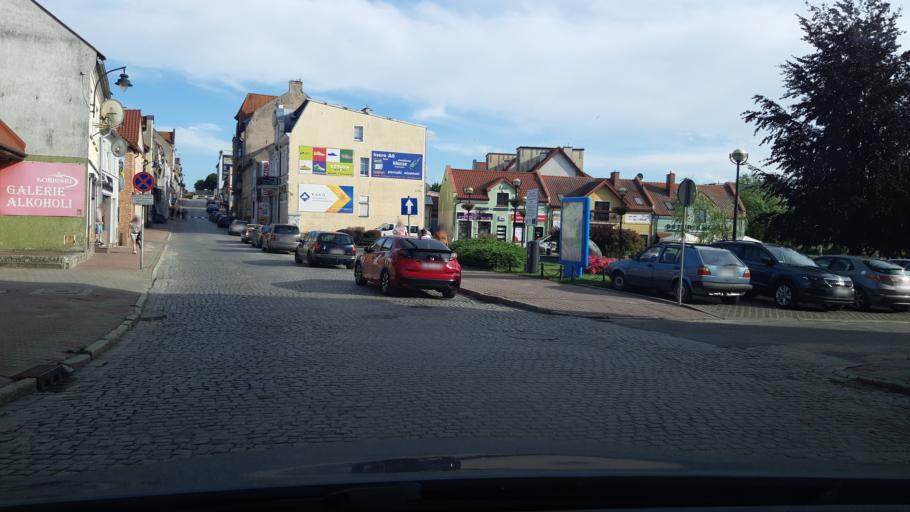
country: PL
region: Warmian-Masurian Voivodeship
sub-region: Powiat mragowski
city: Mragowo
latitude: 53.8695
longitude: 21.3043
